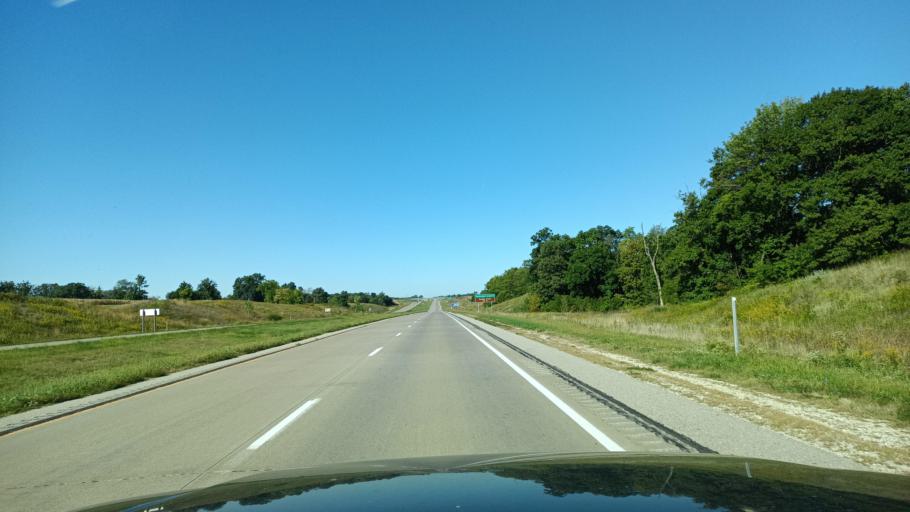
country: US
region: Iowa
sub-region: Lee County
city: Fort Madison
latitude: 40.6707
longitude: -91.3079
